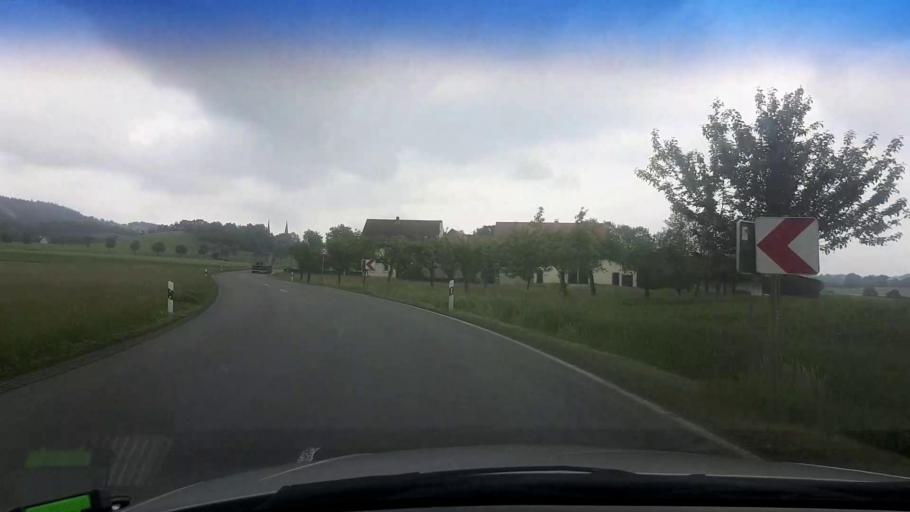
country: DE
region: Bavaria
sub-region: Upper Franconia
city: Goldkronach
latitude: 50.0013
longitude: 11.6807
